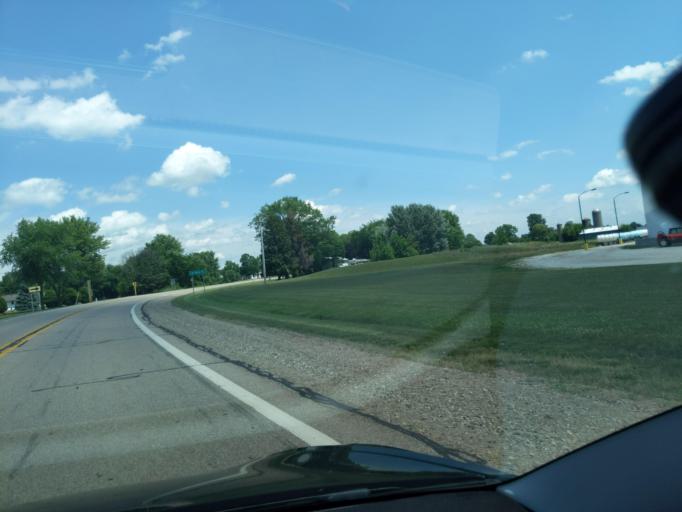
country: US
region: Michigan
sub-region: Clinton County
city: Fowler
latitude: 42.9997
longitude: -84.8400
